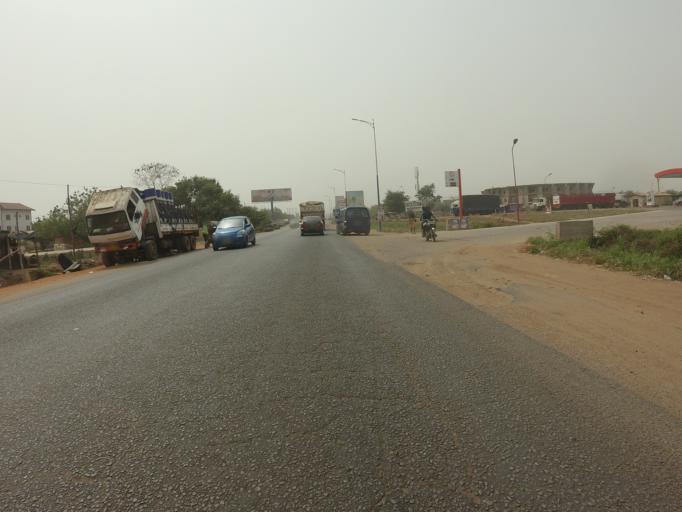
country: GH
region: Greater Accra
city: Tema
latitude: 5.7183
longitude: 0.0165
